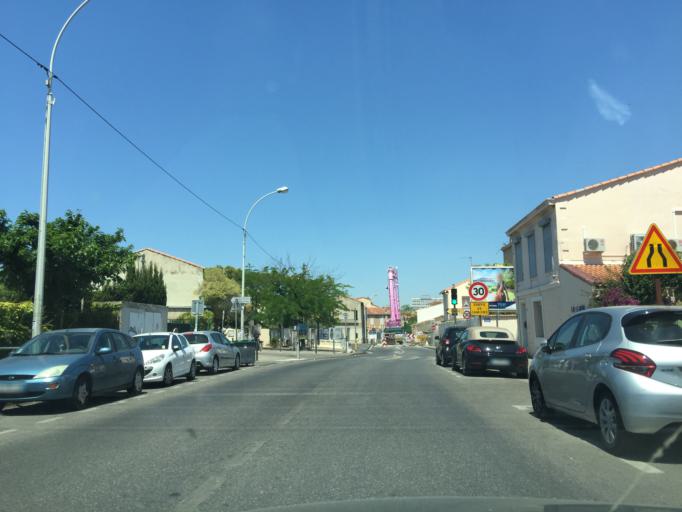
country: FR
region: Provence-Alpes-Cote d'Azur
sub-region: Departement des Bouches-du-Rhone
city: Marseille 09
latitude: 43.2549
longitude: 5.3941
